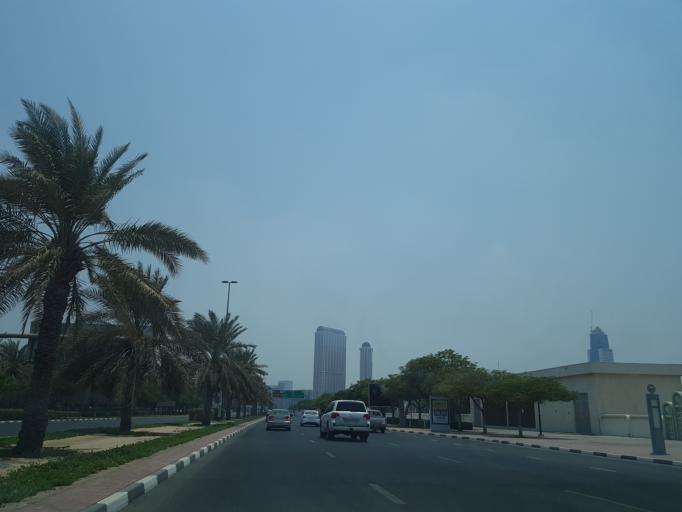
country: AE
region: Ash Shariqah
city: Sharjah
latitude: 25.2440
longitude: 55.3224
